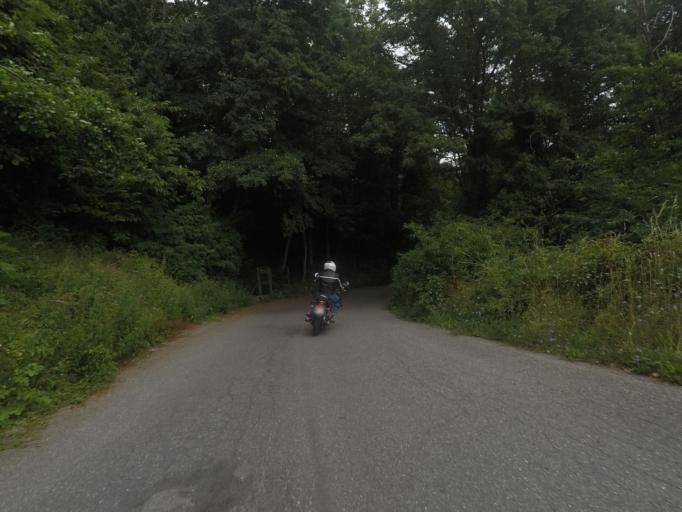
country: IT
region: Tuscany
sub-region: Provincia di Lucca
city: Careggine
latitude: 44.1100
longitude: 10.3595
